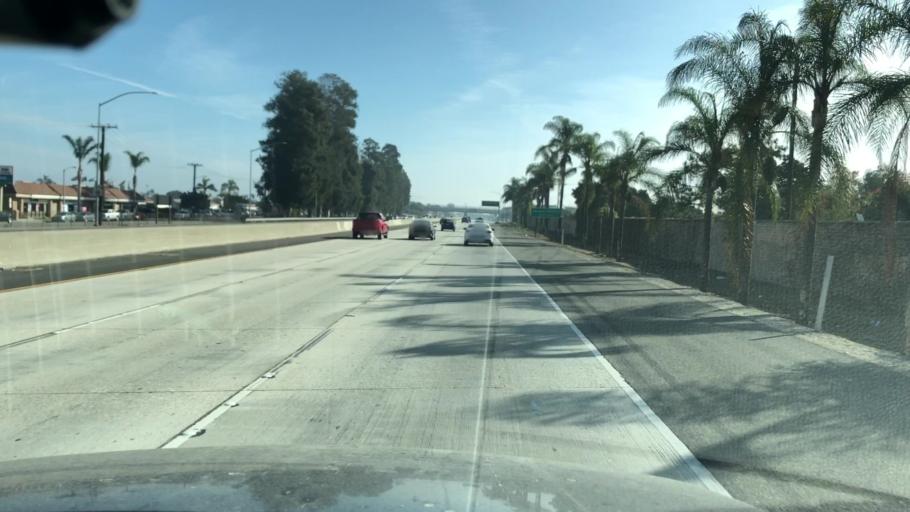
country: US
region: California
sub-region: Ventura County
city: El Rio
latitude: 34.2270
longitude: -119.1663
